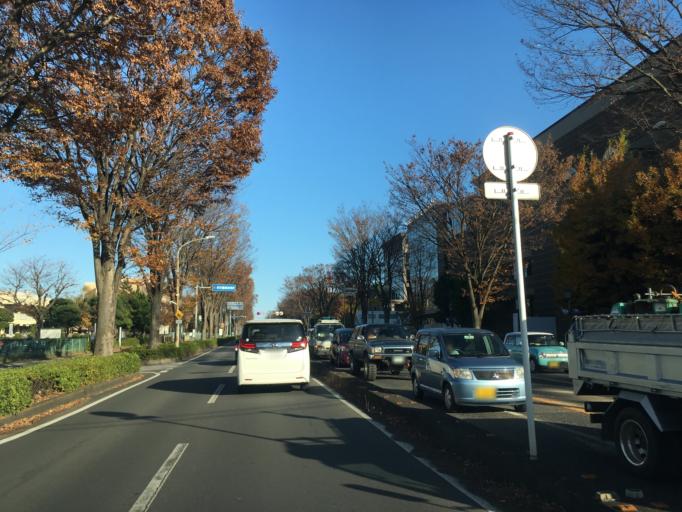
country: JP
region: Saitama
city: Tokorozawa
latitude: 35.8010
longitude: 139.4723
